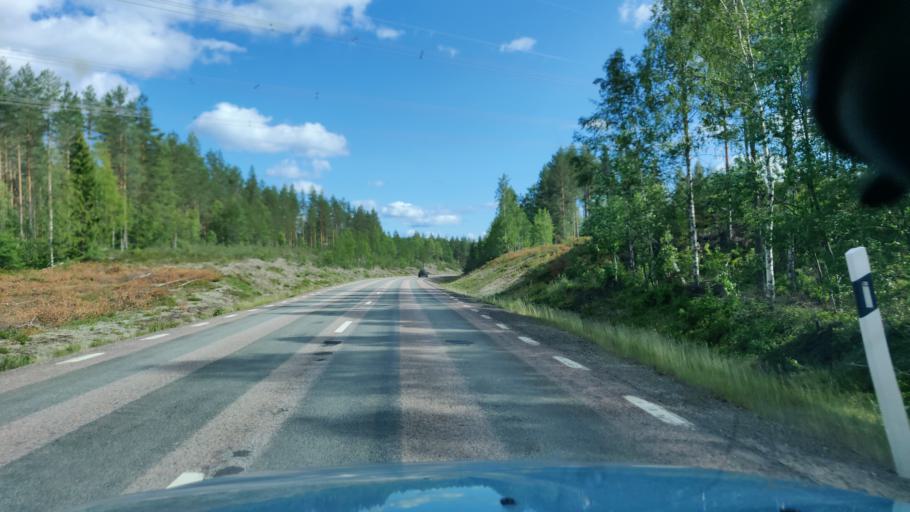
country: SE
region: Vaermland
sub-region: Torsby Kommun
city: Torsby
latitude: 60.5313
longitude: 13.1276
